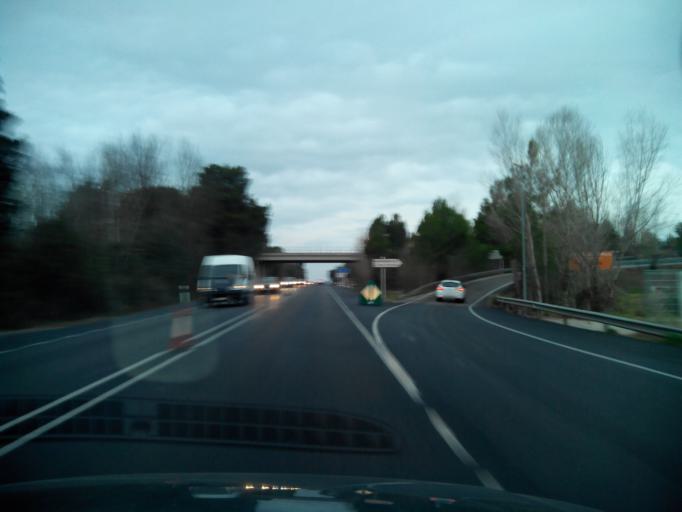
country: ES
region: Catalonia
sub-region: Provincia de Barcelona
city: Olesa de Montserrat
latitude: 41.5879
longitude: 1.9152
